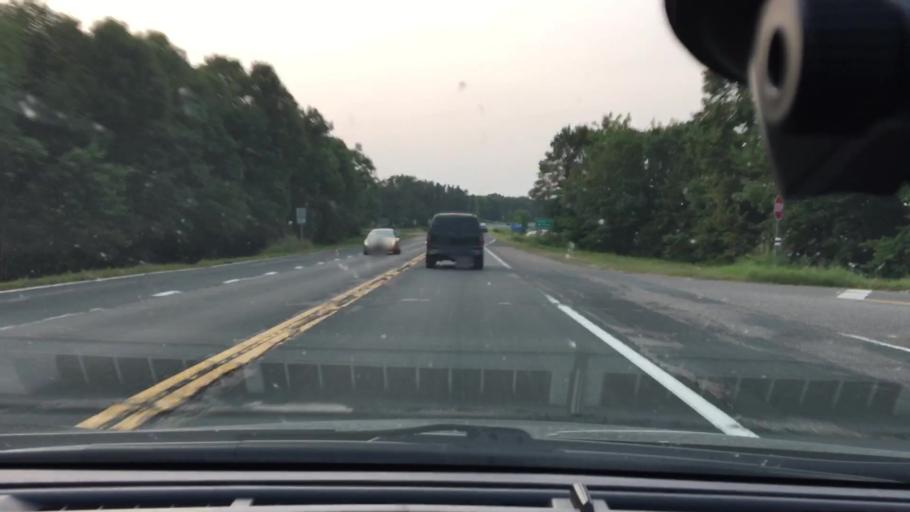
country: US
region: Minnesota
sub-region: Mille Lacs County
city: Vineland
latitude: 46.2062
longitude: -93.7859
